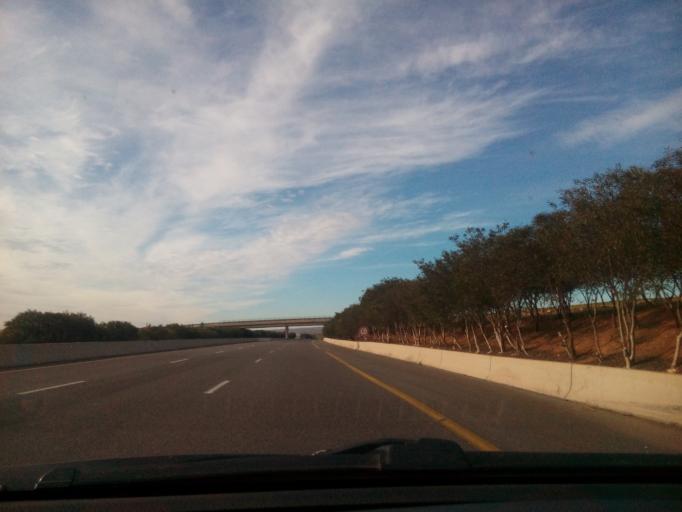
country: DZ
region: Sidi Bel Abbes
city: Sidi Bel Abbes
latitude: 35.1905
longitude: -0.7071
